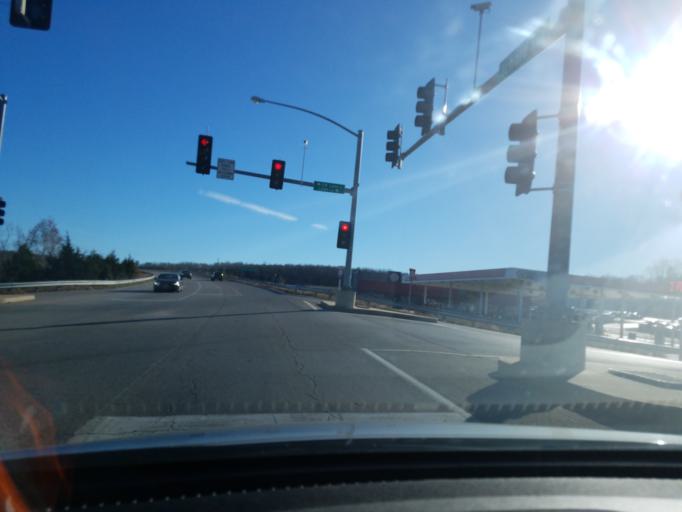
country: US
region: Missouri
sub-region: Pulaski County
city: Waynesville
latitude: 37.8080
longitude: -92.2235
